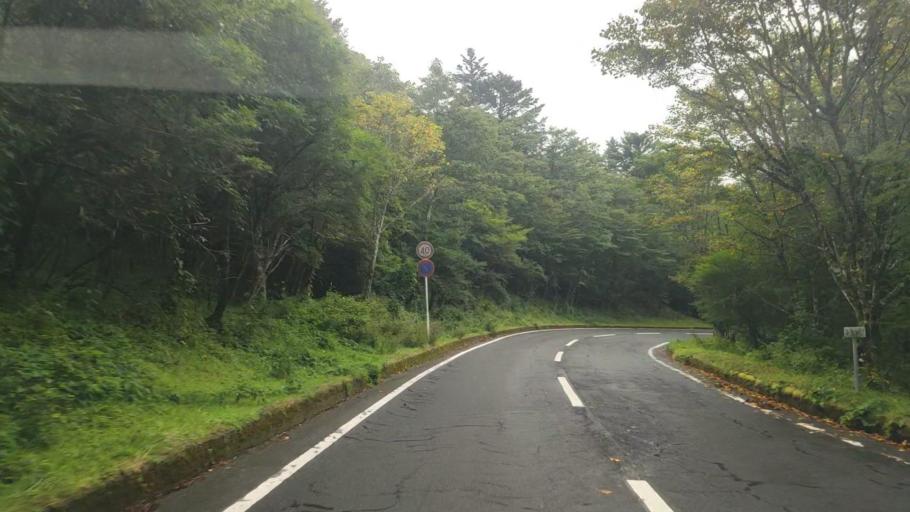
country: JP
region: Shizuoka
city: Fuji
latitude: 35.3092
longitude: 138.7430
